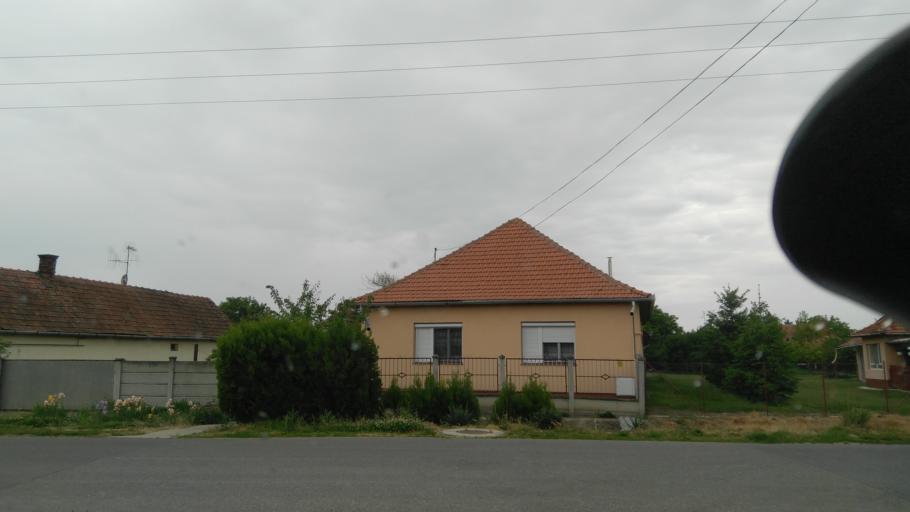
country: HU
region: Bekes
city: Doboz
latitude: 46.7267
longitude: 21.2409
